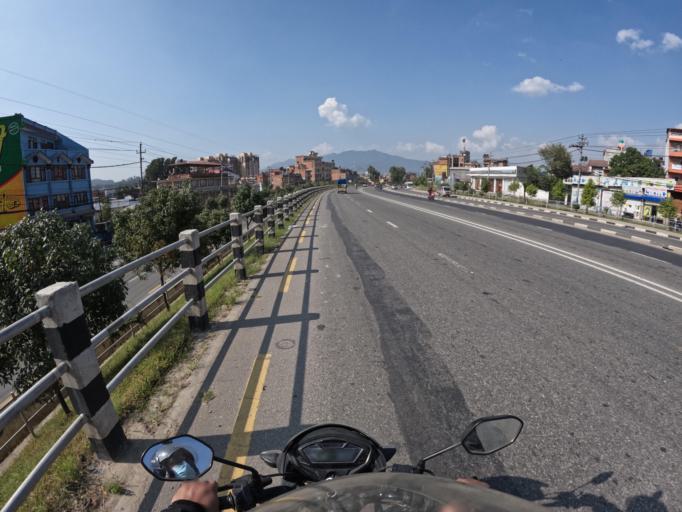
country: NP
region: Central Region
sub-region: Bagmati Zone
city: Patan
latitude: 27.6733
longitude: 85.3028
